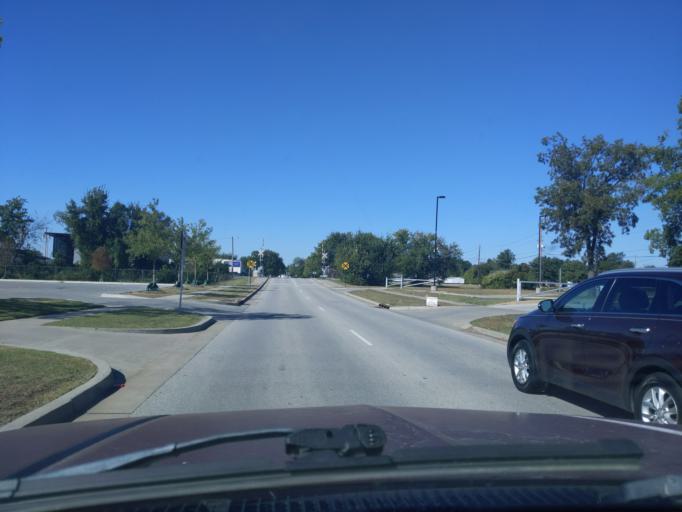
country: US
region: Oklahoma
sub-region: Tulsa County
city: Jenks
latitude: 36.0236
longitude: -95.9699
